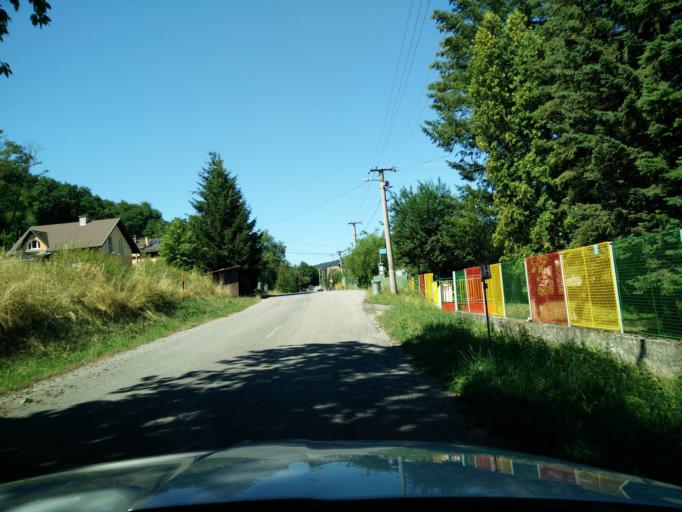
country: SK
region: Nitriansky
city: Prievidza
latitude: 48.7889
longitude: 18.6992
